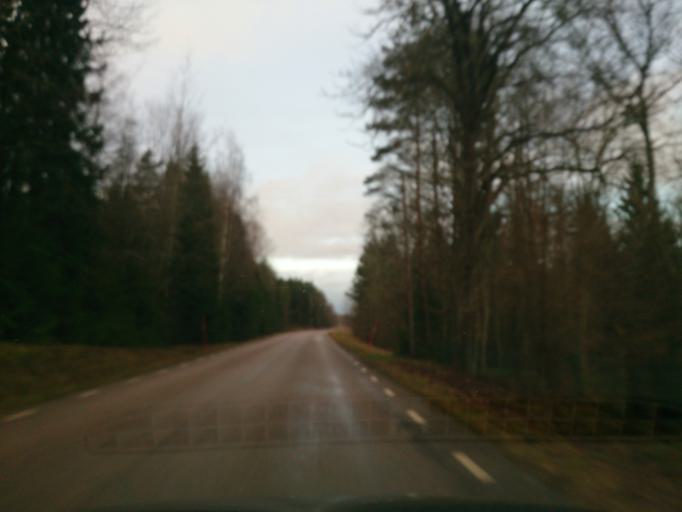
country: SE
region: OEstergoetland
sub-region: Atvidabergs Kommun
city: Atvidaberg
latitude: 58.3201
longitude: 16.0271
